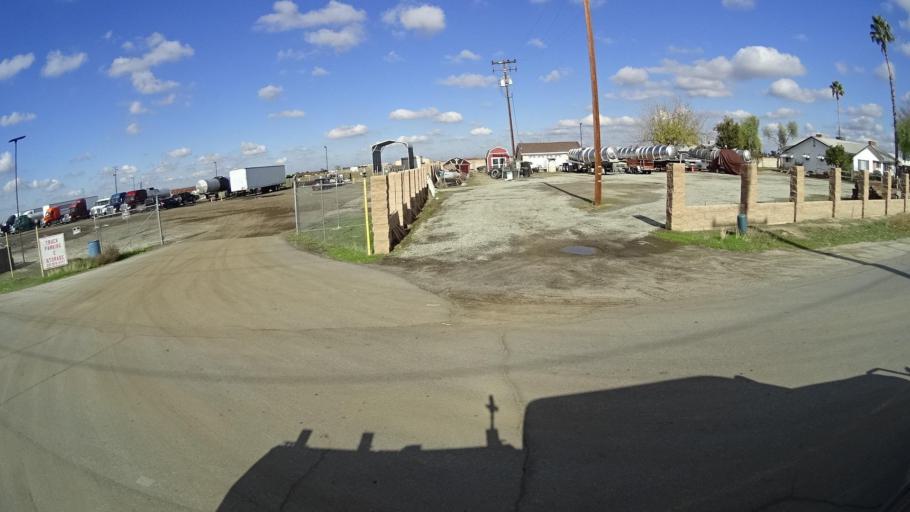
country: US
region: California
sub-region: Kern County
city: McFarland
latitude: 35.6744
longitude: -119.2445
